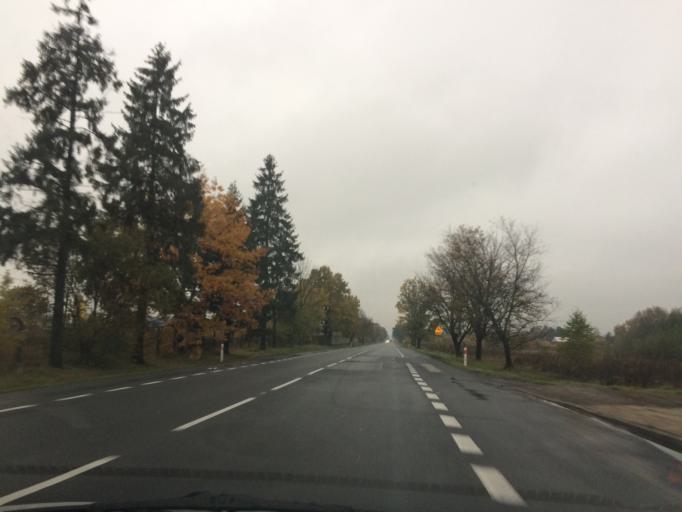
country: PL
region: Masovian Voivodeship
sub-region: Powiat otwocki
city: Celestynow
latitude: 52.0907
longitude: 21.4203
